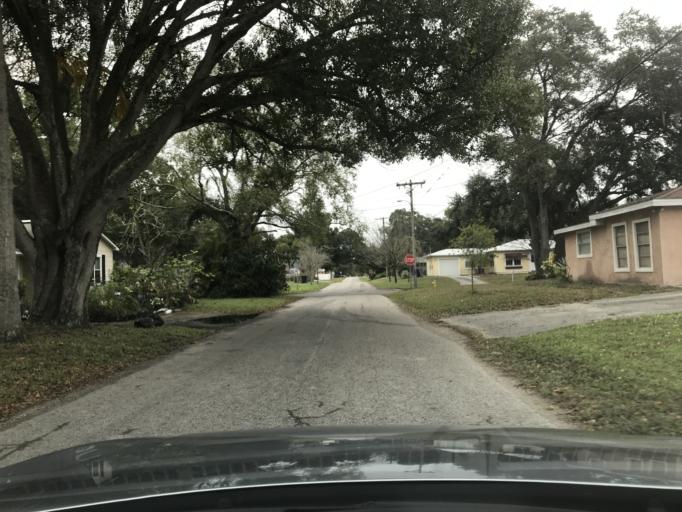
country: US
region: Florida
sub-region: Hillsborough County
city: Tampa
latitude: 27.9766
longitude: -82.4736
